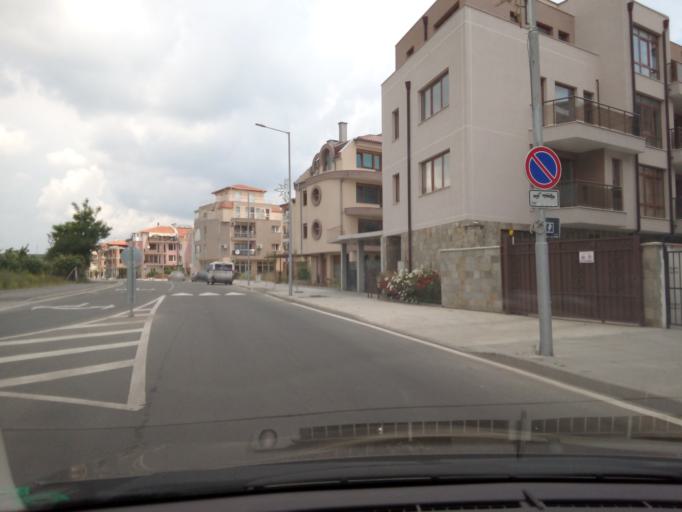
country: BG
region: Burgas
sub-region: Obshtina Nesebur
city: Ravda
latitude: 42.6534
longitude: 27.7024
